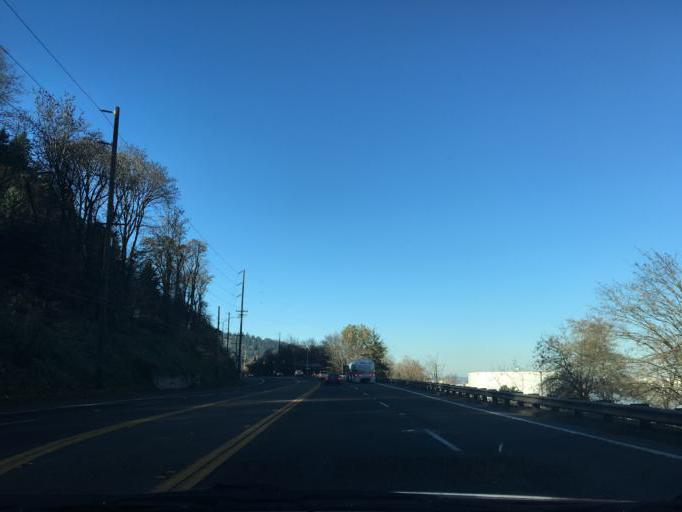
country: US
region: Oregon
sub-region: Washington County
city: West Haven
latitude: 45.5861
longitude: -122.7716
